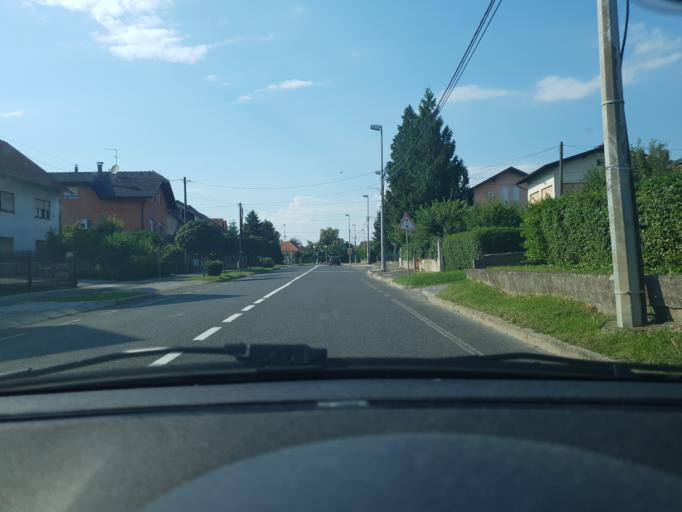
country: HR
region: Zagrebacka
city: Zapresic
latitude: 45.8635
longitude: 15.8026
